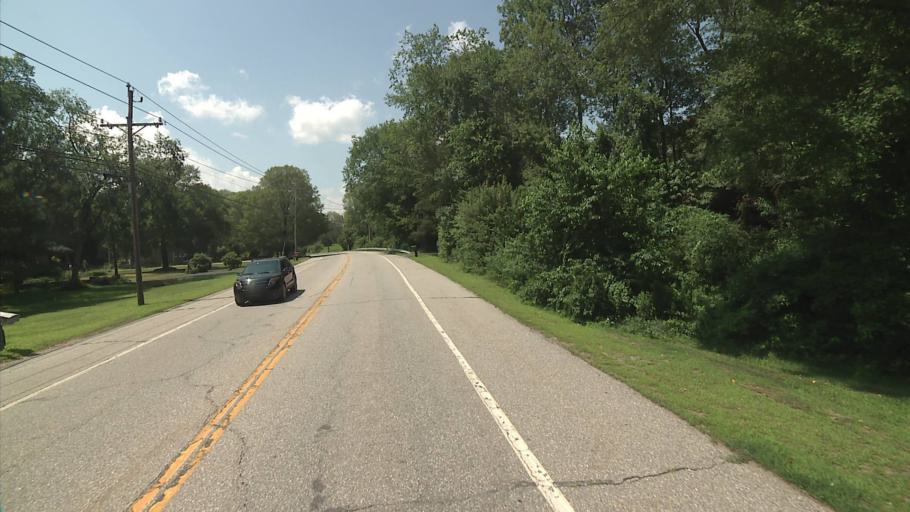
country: US
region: Connecticut
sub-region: New London County
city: Norwich
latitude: 41.5360
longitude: -72.0283
